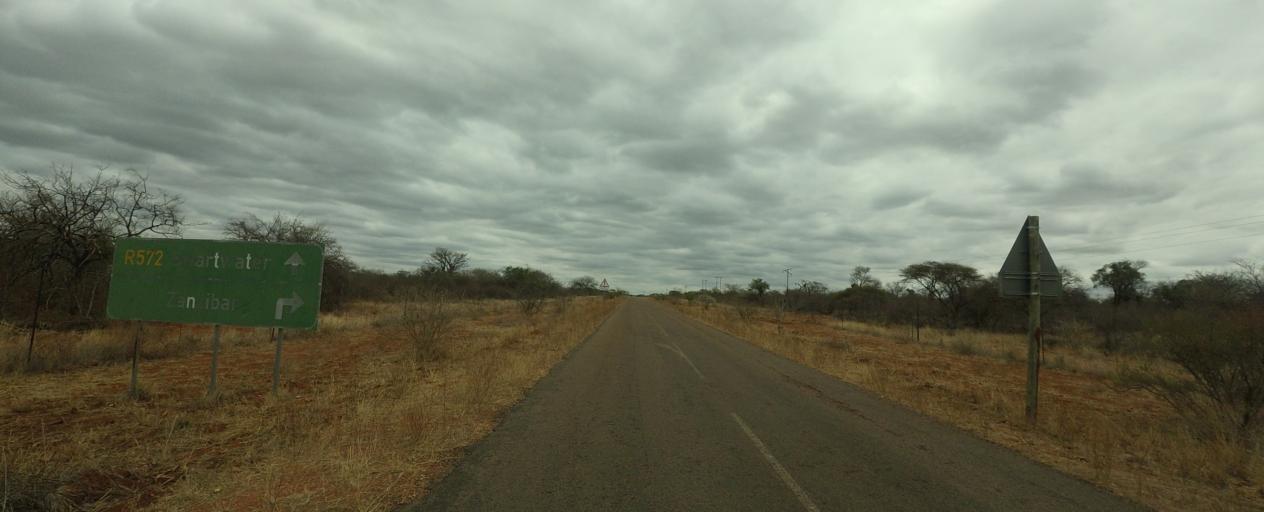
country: BW
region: Central
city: Mathathane
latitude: -22.7391
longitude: 28.4657
